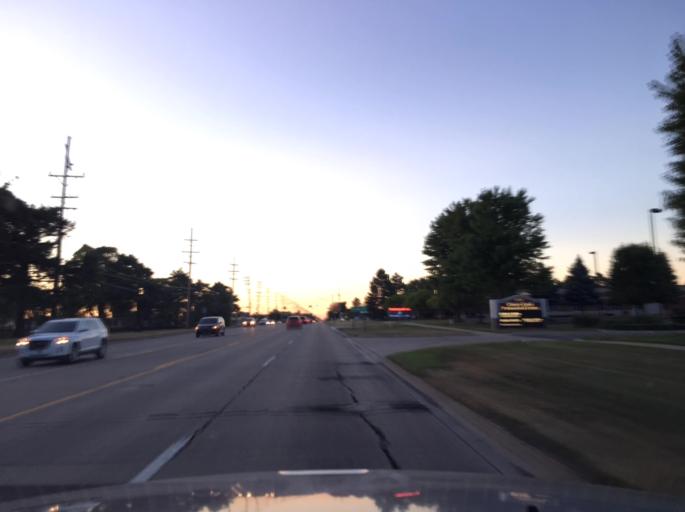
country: US
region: Michigan
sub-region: Macomb County
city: Clinton
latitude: 42.5818
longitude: -82.9517
